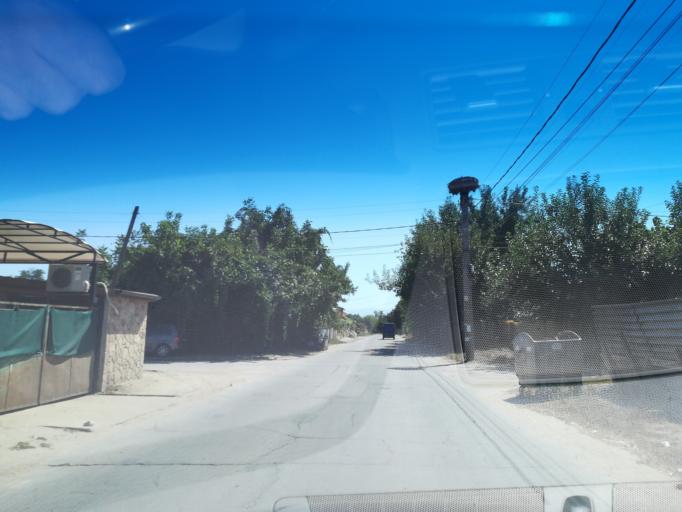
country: BG
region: Pazardzhik
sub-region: Obshtina Pazardzhik
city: Pazardzhik
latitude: 42.2775
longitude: 24.3956
